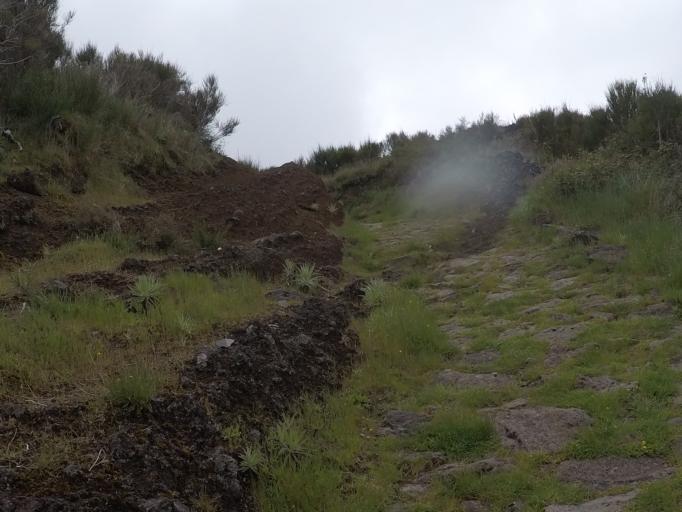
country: PT
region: Madeira
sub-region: Camara de Lobos
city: Curral das Freiras
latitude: 32.7172
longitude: -16.9900
